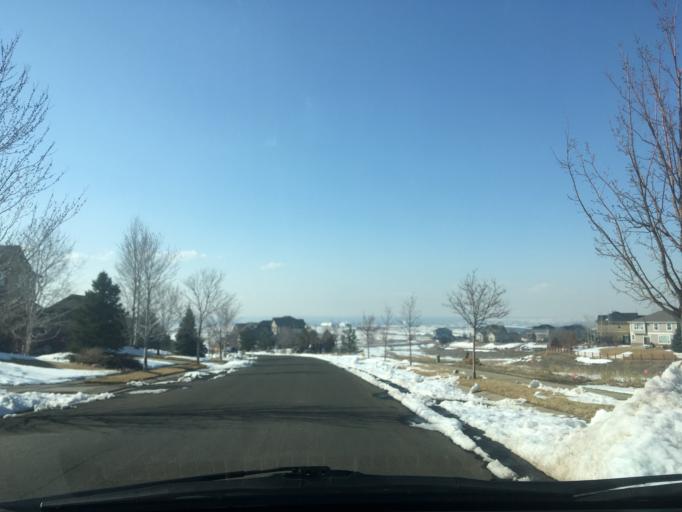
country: US
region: Colorado
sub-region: Boulder County
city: Lafayette
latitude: 39.9680
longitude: -105.0516
